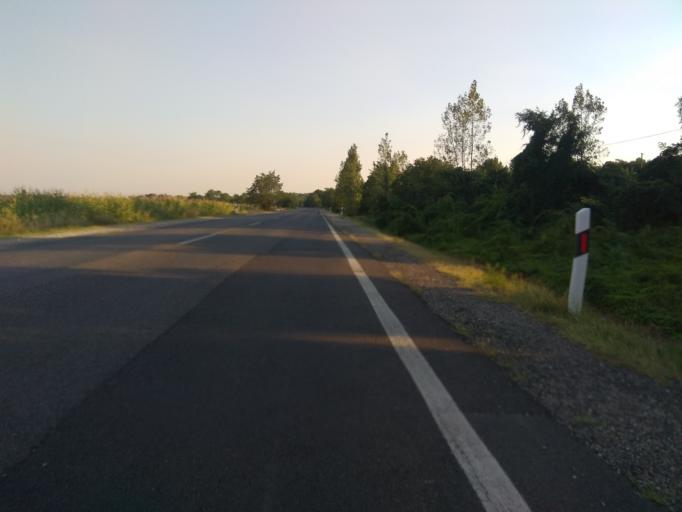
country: HU
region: Borsod-Abauj-Zemplen
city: Nyekladhaza
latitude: 47.9796
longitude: 20.8305
